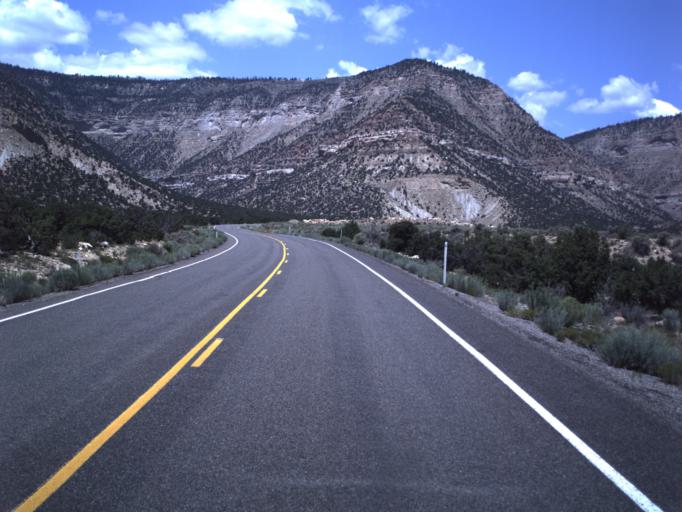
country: US
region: Utah
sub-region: Emery County
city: Orangeville
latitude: 39.2950
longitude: -111.1122
